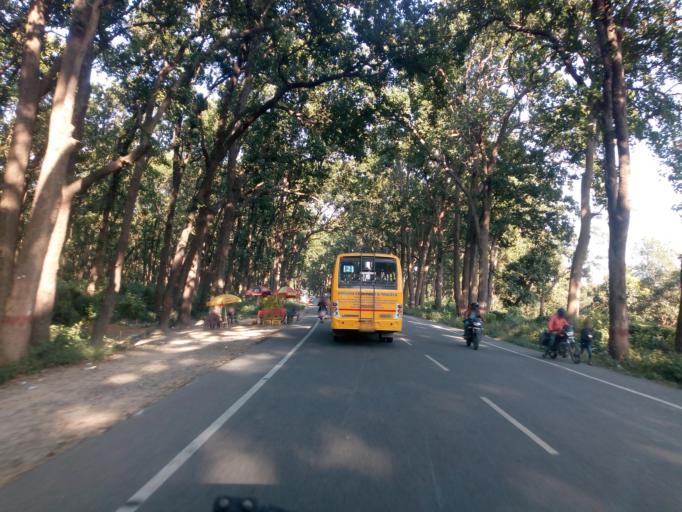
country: IN
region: Uttarakhand
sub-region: Dehradun
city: Dehradun
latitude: 30.3474
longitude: 77.8812
